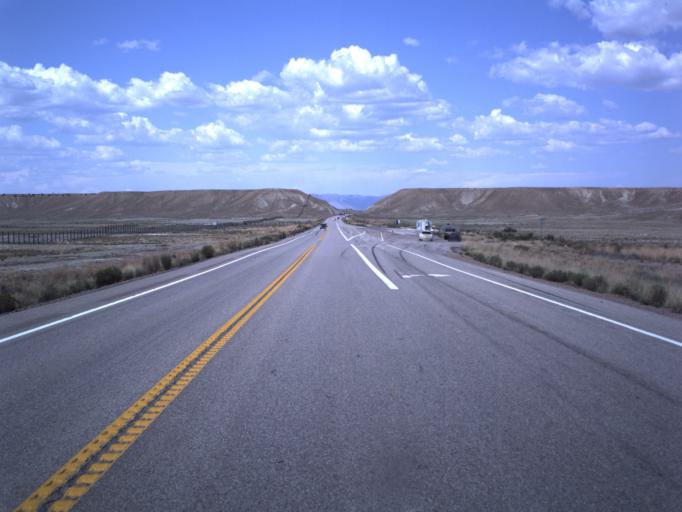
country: US
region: Utah
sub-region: Carbon County
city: Price
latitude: 39.4547
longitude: -110.8614
